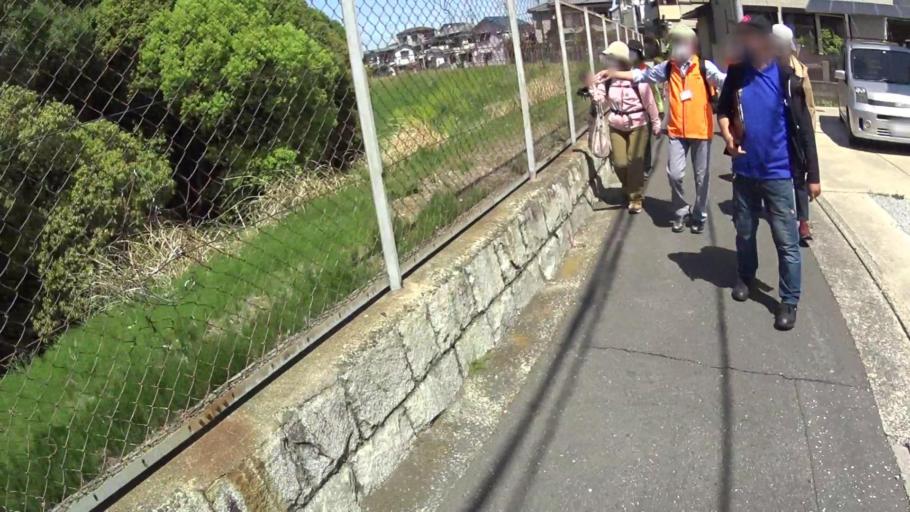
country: JP
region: Osaka
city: Kashihara
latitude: 34.5705
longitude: 135.6144
